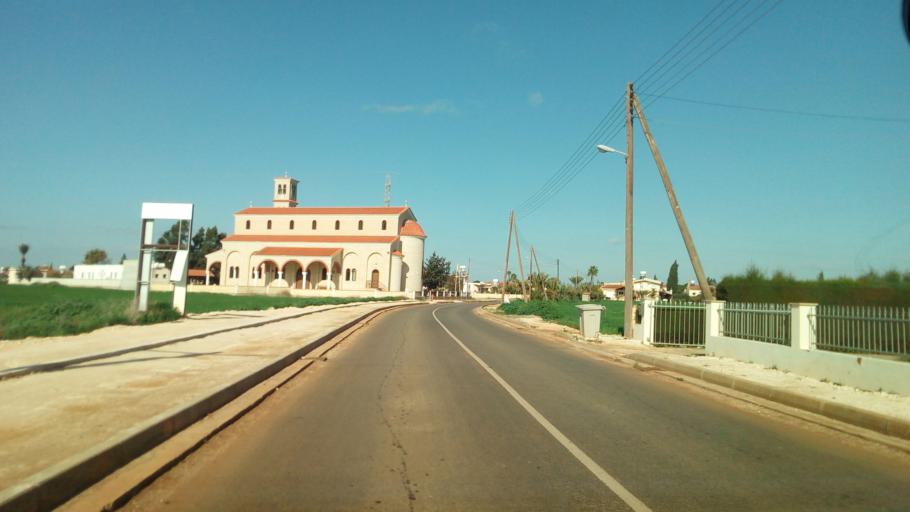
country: CY
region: Ammochostos
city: Avgorou
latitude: 35.0238
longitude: 33.8403
